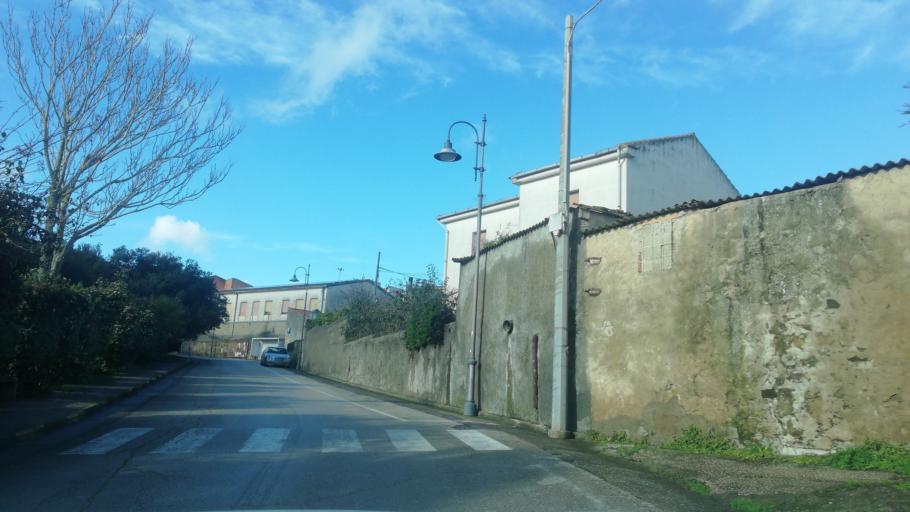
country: IT
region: Sardinia
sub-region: Provincia di Medio Campidano
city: Villanovaforru
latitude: 39.6310
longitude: 8.8729
